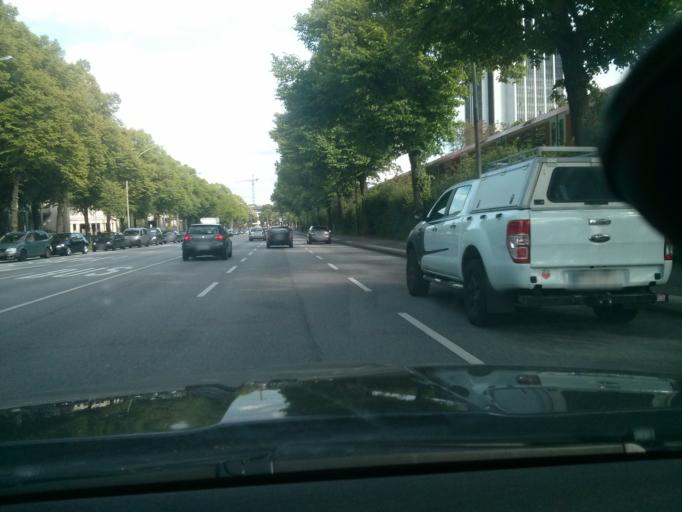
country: DE
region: Hamburg
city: Eimsbuettel
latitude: 53.5635
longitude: 9.9859
